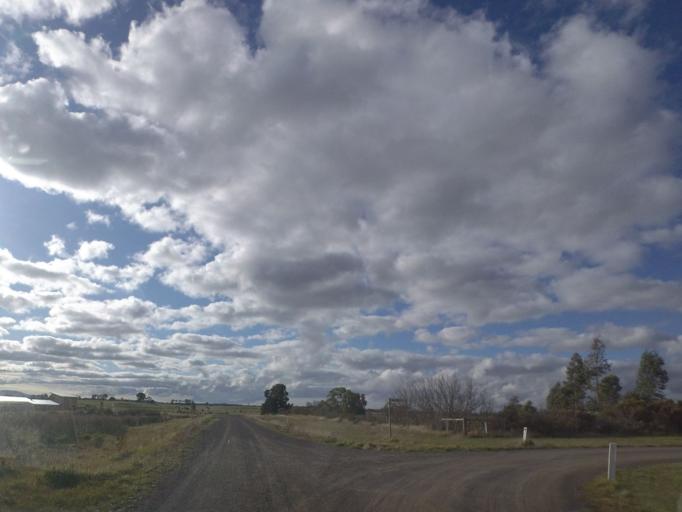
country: AU
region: Victoria
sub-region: Mount Alexander
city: Castlemaine
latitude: -37.1853
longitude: 144.3912
